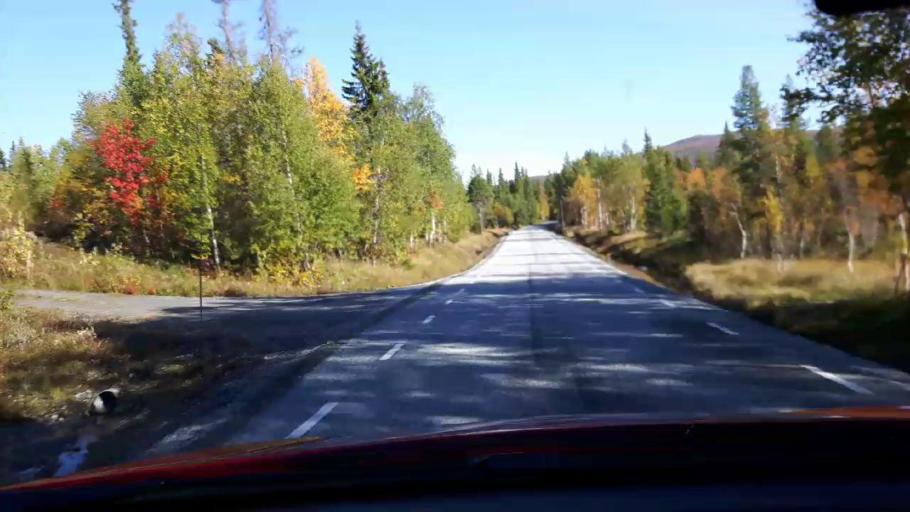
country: NO
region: Nord-Trondelag
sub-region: Royrvik
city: Royrvik
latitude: 64.8162
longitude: 14.2095
